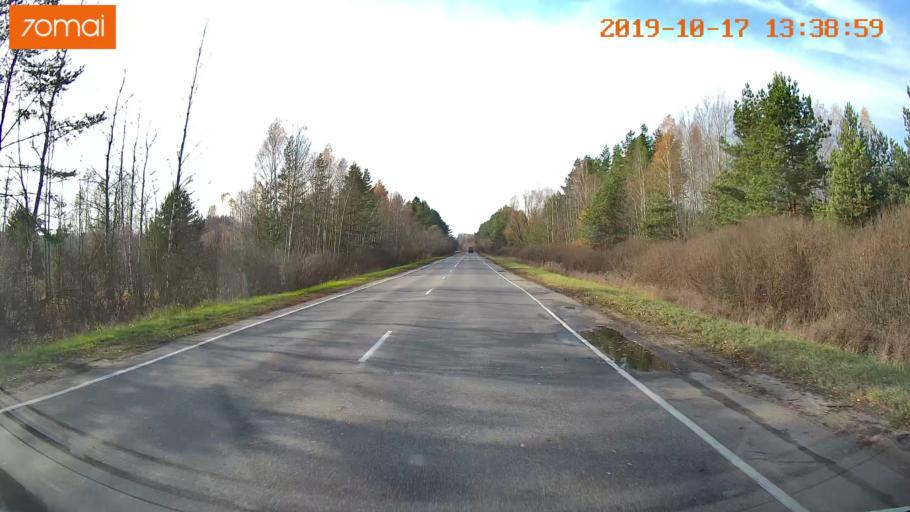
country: RU
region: Rjazan
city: Tuma
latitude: 55.1452
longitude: 40.5993
